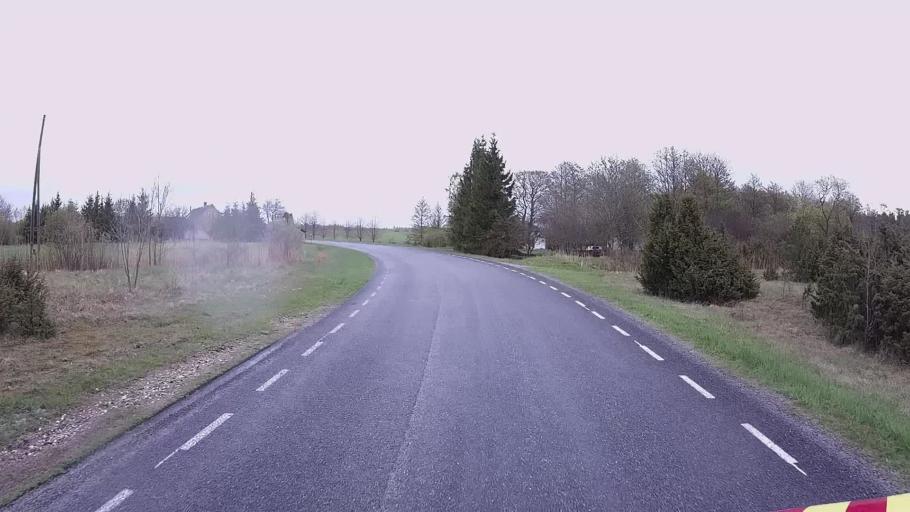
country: EE
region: Hiiumaa
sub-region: Kaerdla linn
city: Kardla
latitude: 58.6960
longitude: 22.5290
